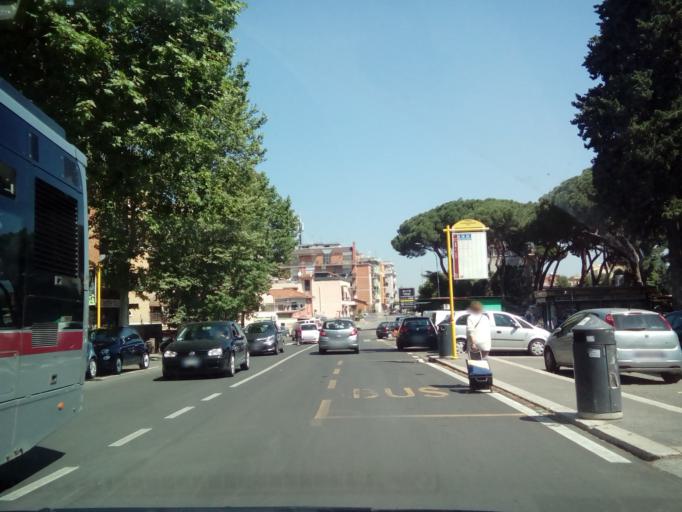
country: IT
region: Latium
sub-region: Citta metropolitana di Roma Capitale
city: Rome
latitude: 41.8804
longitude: 12.5776
